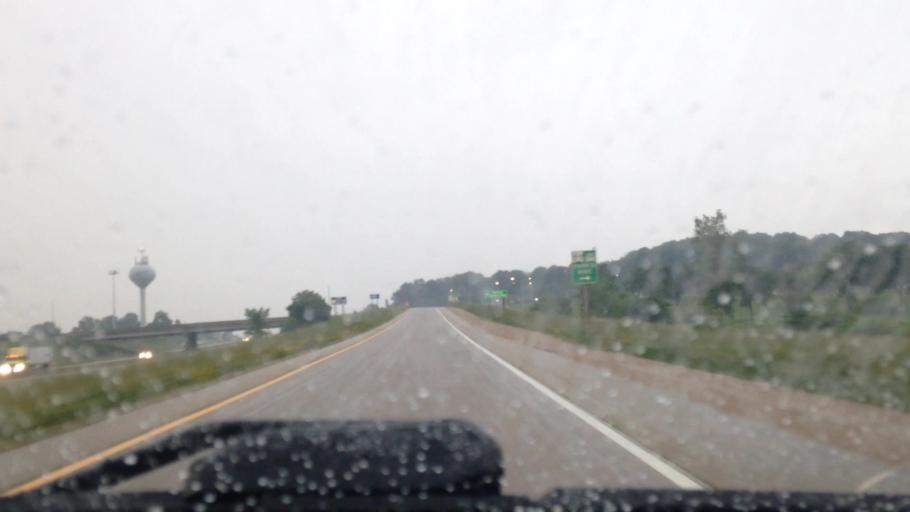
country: US
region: Wisconsin
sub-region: Washington County
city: Slinger
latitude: 43.4214
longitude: -88.3343
